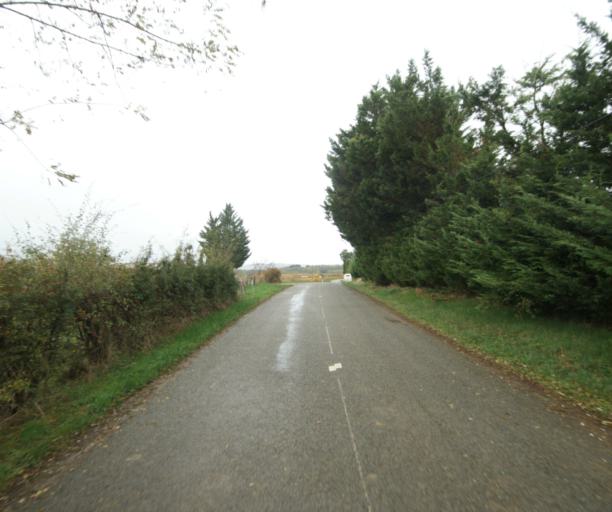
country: FR
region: Rhone-Alpes
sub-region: Departement de l'Ain
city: Pont-de-Vaux
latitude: 46.4774
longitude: 4.8629
